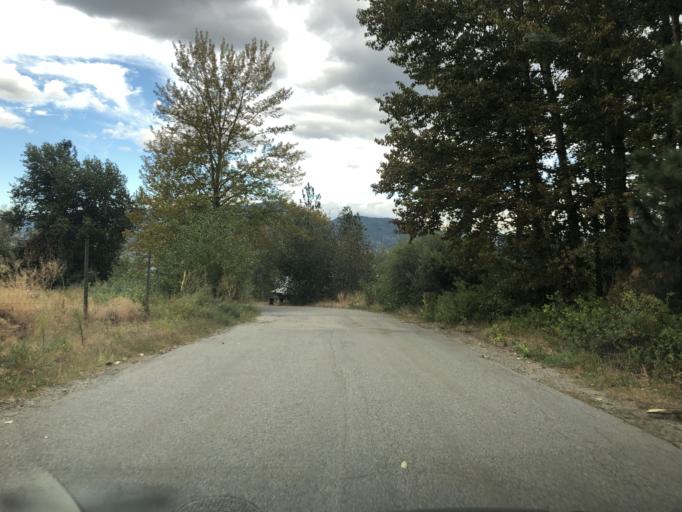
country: CA
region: British Columbia
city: Penticton
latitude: 49.5472
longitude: -119.5672
